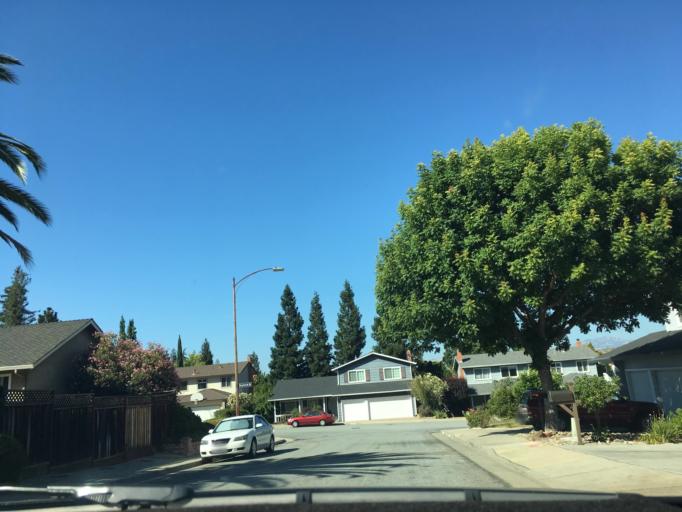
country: US
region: California
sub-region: Santa Clara County
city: Cambrian Park
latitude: 37.2175
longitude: -121.8840
